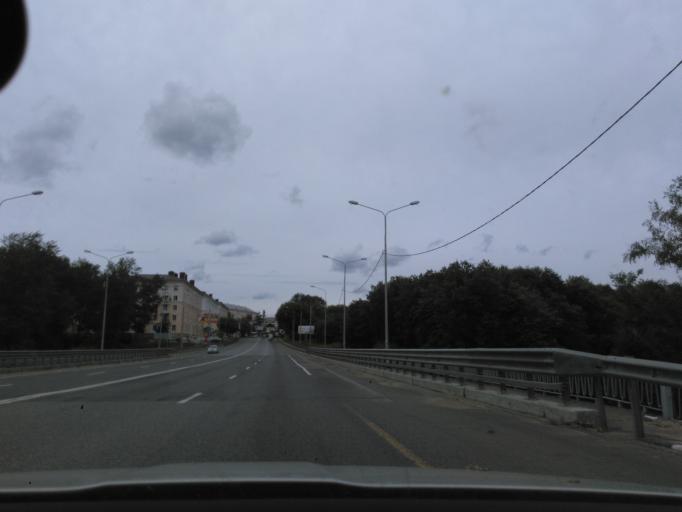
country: RU
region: Moskovskaya
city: Klin
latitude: 56.3294
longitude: 36.7372
